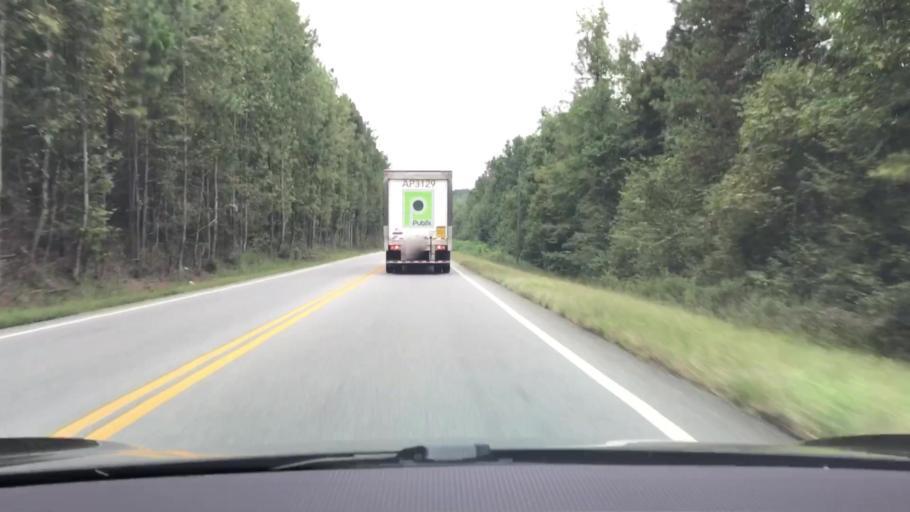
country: US
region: Georgia
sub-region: Greene County
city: Greensboro
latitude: 33.6867
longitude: -83.2741
